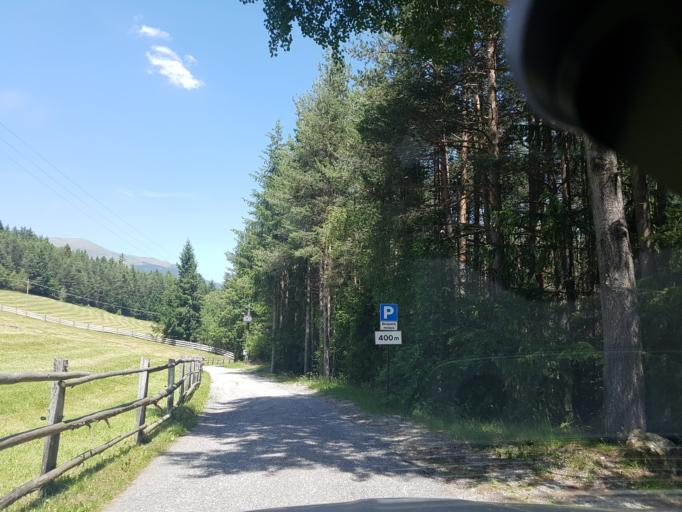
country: IT
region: Trentino-Alto Adige
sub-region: Bolzano
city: Villandro
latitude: 46.6479
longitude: 11.5392
